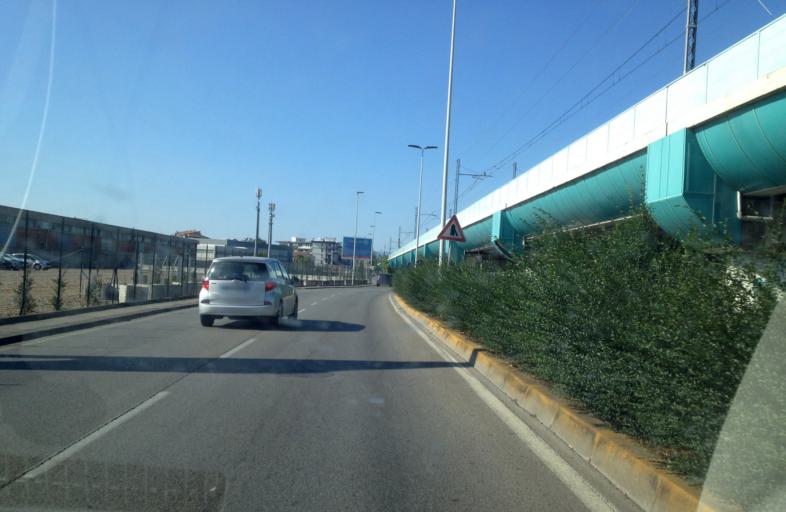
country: IT
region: Tuscany
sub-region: Province of Florence
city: Sesto Fiorentino
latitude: 43.8002
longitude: 11.1994
